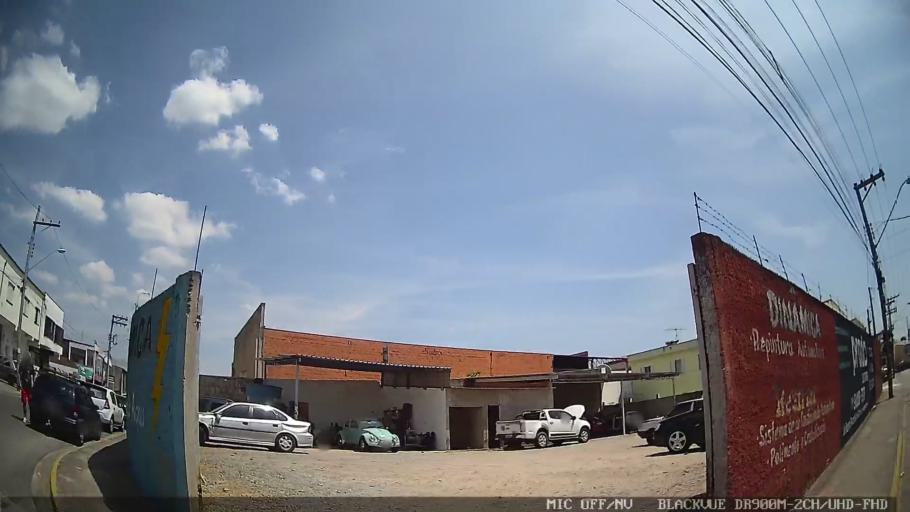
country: BR
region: Sao Paulo
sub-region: Itupeva
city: Itupeva
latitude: -23.2448
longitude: -47.0590
